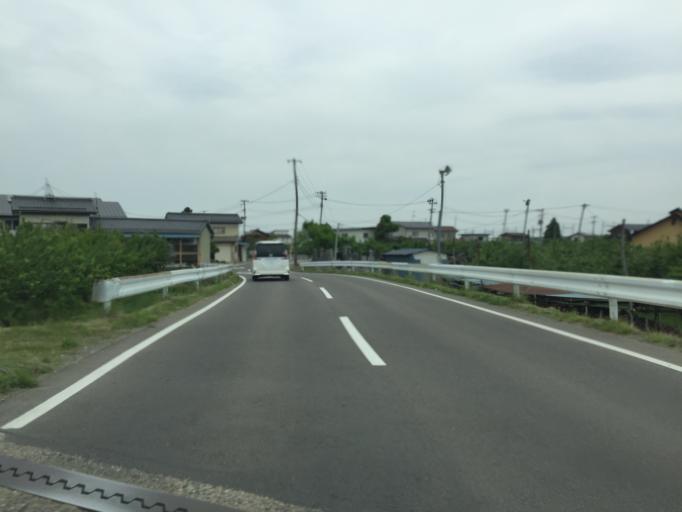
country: JP
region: Fukushima
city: Fukushima-shi
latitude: 37.7955
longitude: 140.4708
